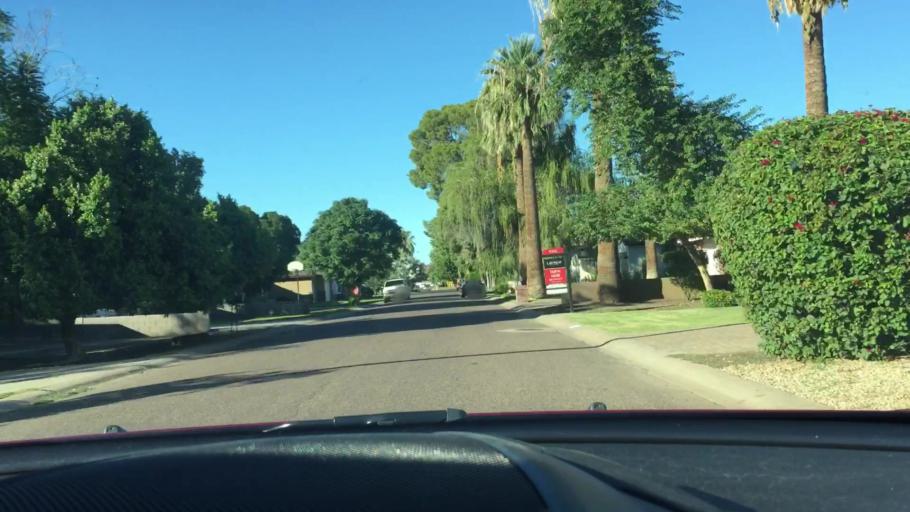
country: US
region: Arizona
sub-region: Maricopa County
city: Paradise Valley
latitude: 33.4817
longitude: -111.9790
